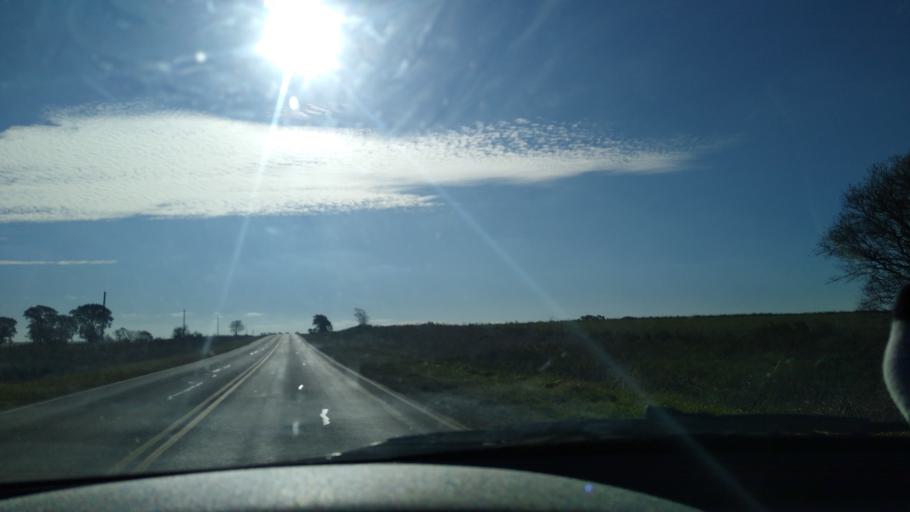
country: AR
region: Entre Rios
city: Aranguren
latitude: -32.3582
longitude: -60.3533
